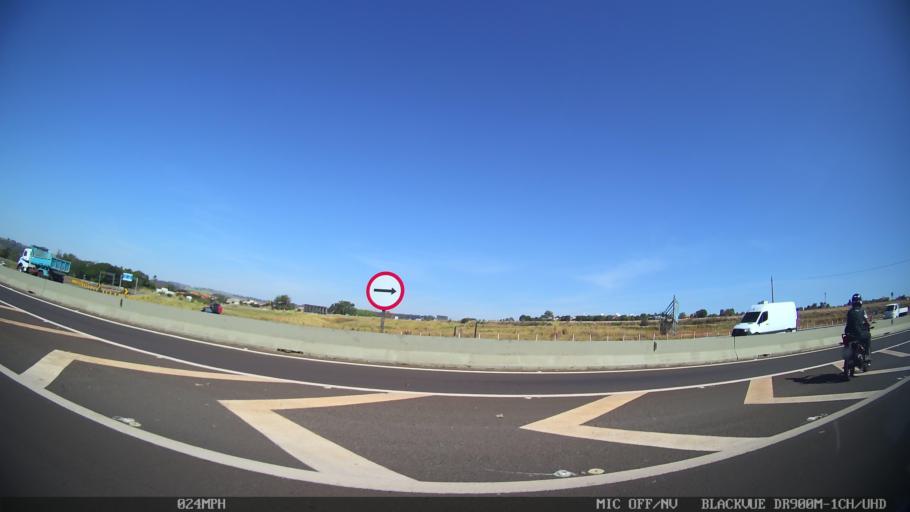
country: BR
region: Sao Paulo
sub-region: Ribeirao Preto
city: Ribeirao Preto
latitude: -21.2223
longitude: -47.7782
